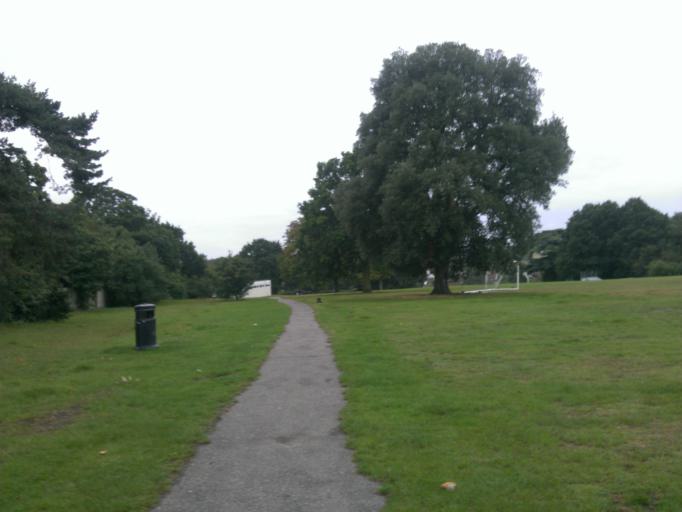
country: GB
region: England
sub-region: Essex
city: Wivenhoe
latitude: 51.8592
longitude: 0.9581
